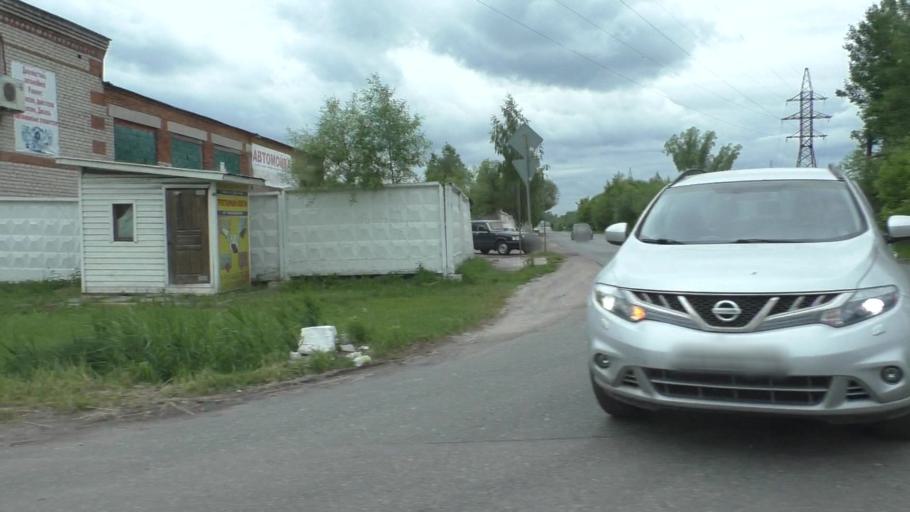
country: RU
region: Moskovskaya
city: Yegor'yevsk
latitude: 55.3973
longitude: 39.0139
